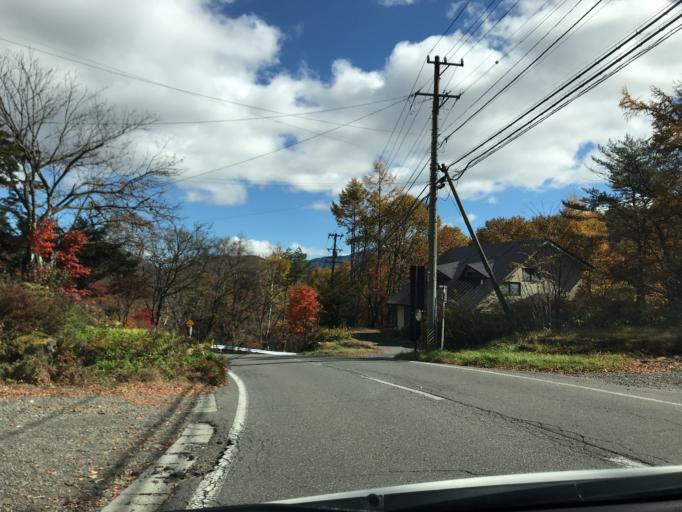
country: JP
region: Nagano
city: Toyoshina
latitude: 36.1237
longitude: 137.6435
